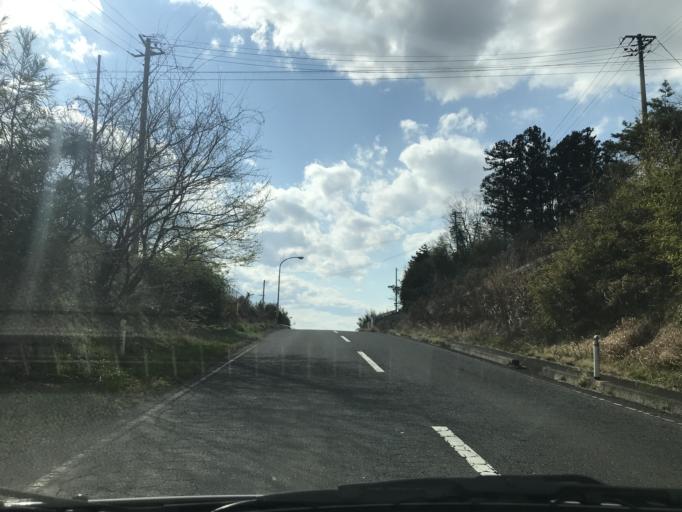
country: JP
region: Iwate
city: Ichinoseki
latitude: 38.7430
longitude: 141.1926
